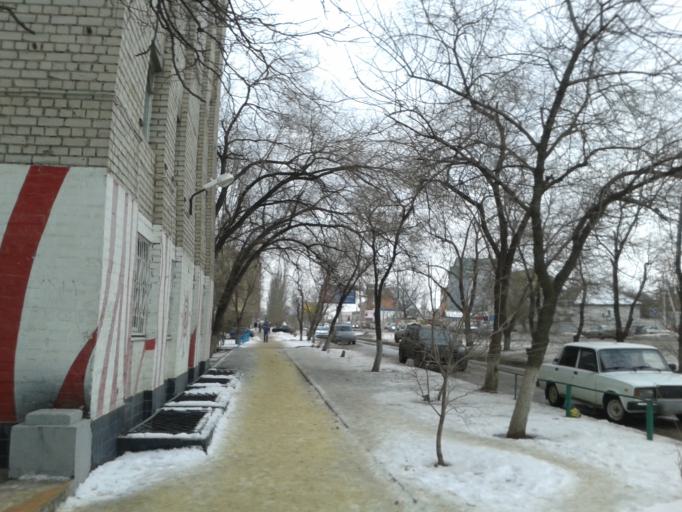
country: RU
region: Volgograd
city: Volgograd
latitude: 48.7254
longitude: 44.5167
